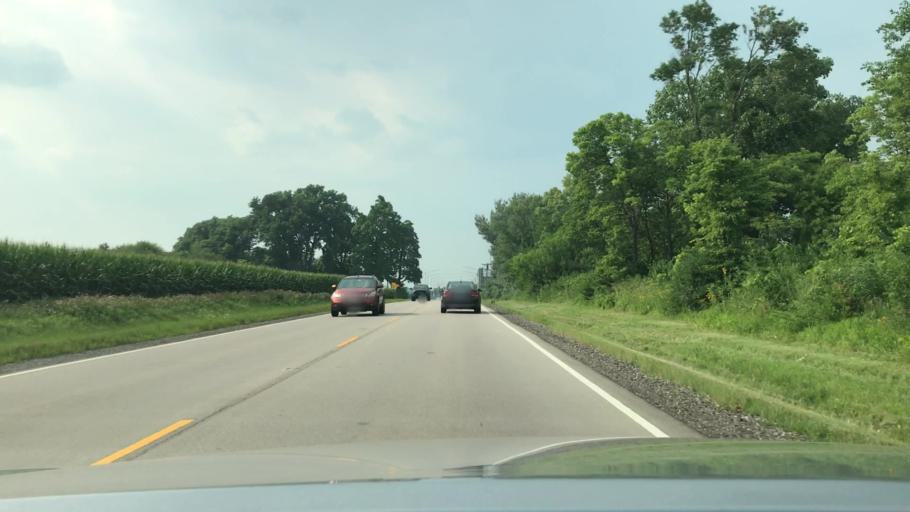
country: US
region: Illinois
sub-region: Will County
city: Plainfield
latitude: 41.6474
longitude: -88.2276
